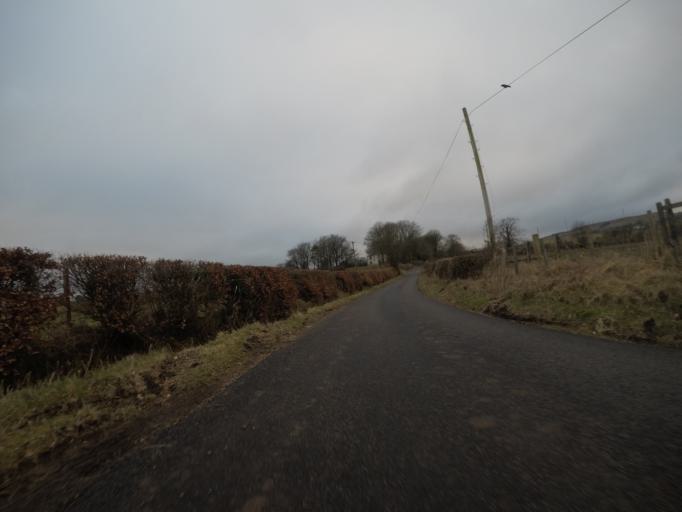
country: GB
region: Scotland
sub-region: North Ayrshire
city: Dalry
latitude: 55.7143
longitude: -4.7545
